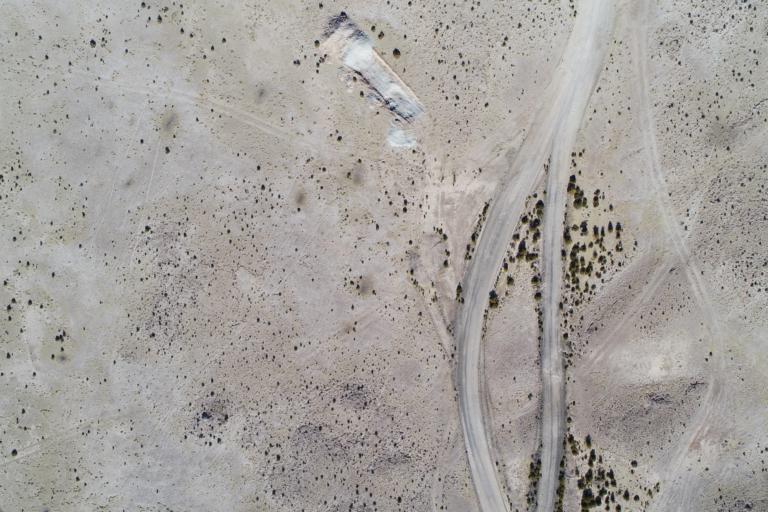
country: BO
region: Potosi
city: Colchani
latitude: -20.3520
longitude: -66.8933
